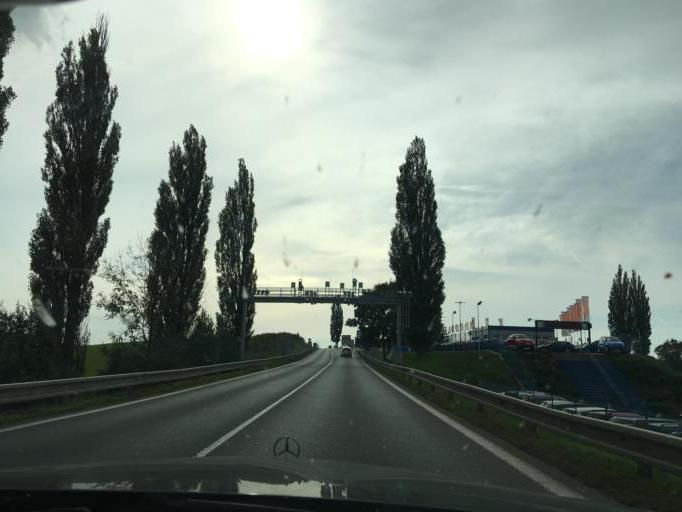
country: CZ
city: Predmerice nad Labem
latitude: 50.2883
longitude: 15.8284
